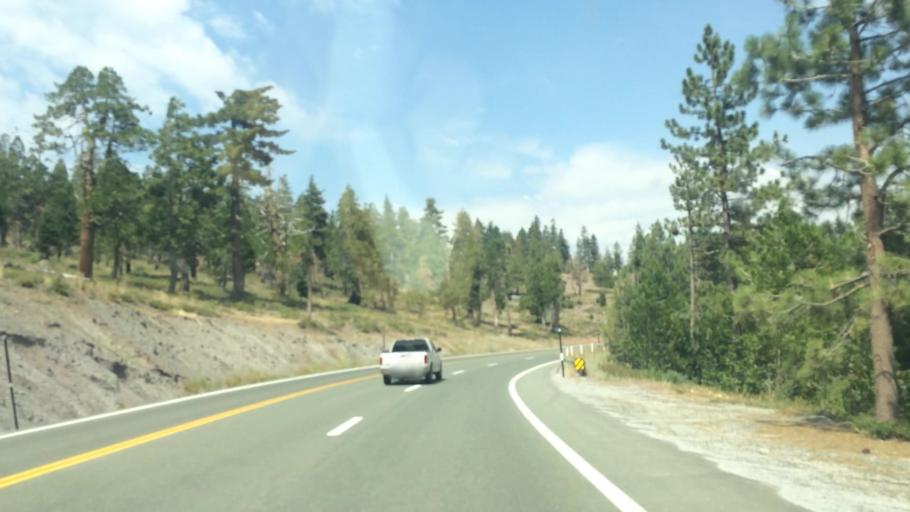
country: US
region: California
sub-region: Amador County
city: Pioneer
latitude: 38.5444
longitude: -120.3156
